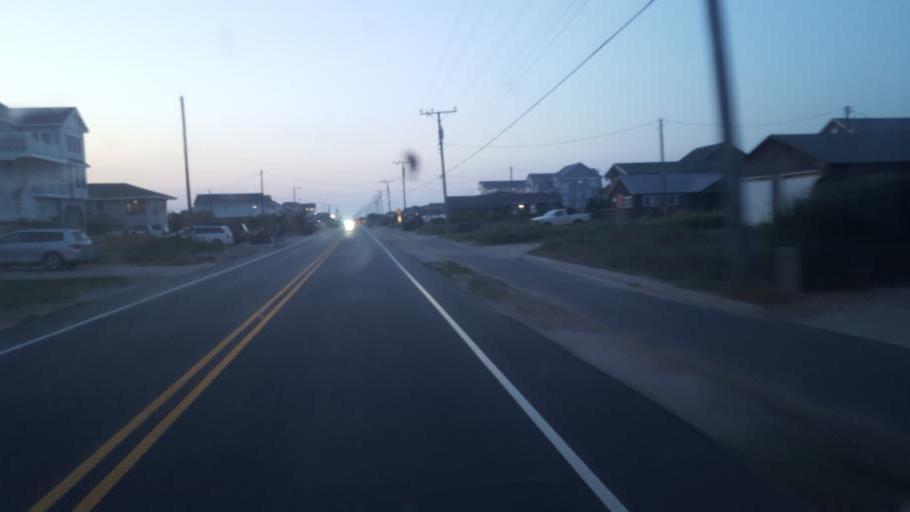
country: US
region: North Carolina
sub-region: Dare County
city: Nags Head
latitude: 35.9749
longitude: -75.6340
